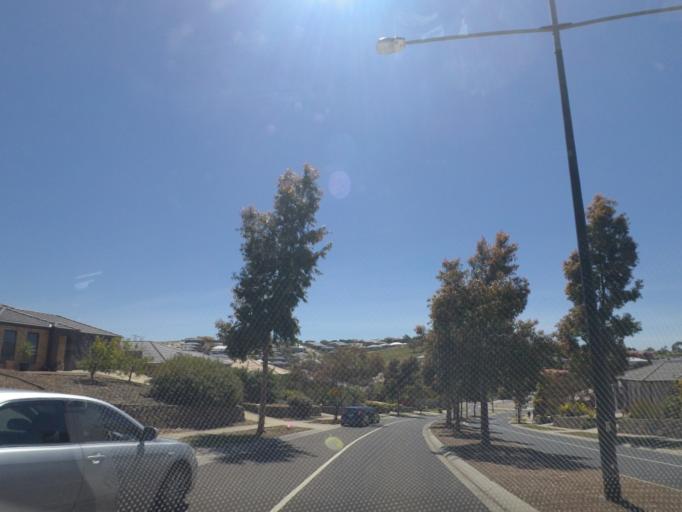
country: AU
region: Victoria
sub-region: Hume
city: Sunbury
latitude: -37.5637
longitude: 144.6988
